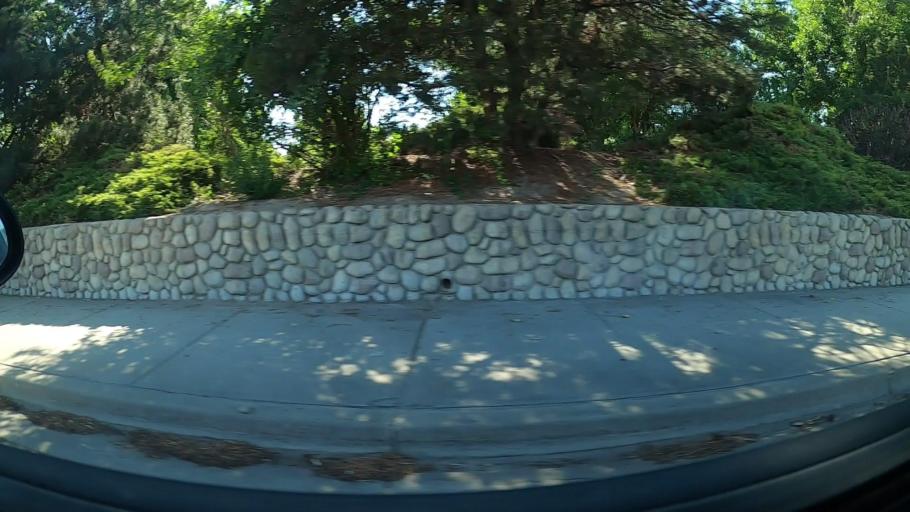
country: US
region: Idaho
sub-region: Ada County
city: Eagle
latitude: 43.6641
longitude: -116.3545
